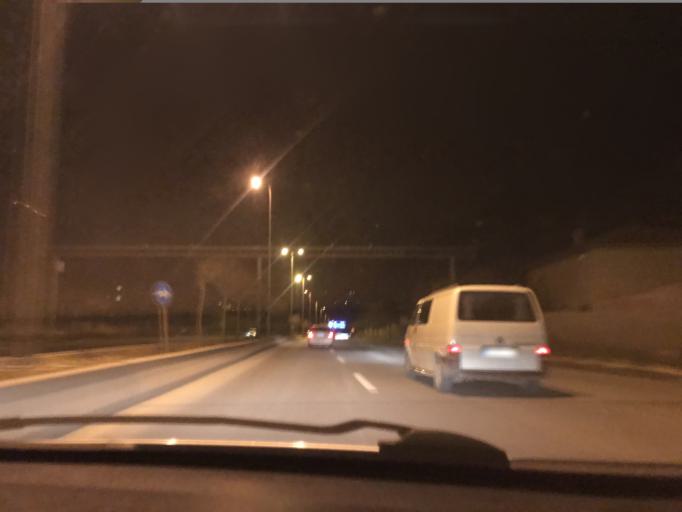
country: TR
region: Ankara
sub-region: Goelbasi
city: Golbasi
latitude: 39.8442
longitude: 32.7948
